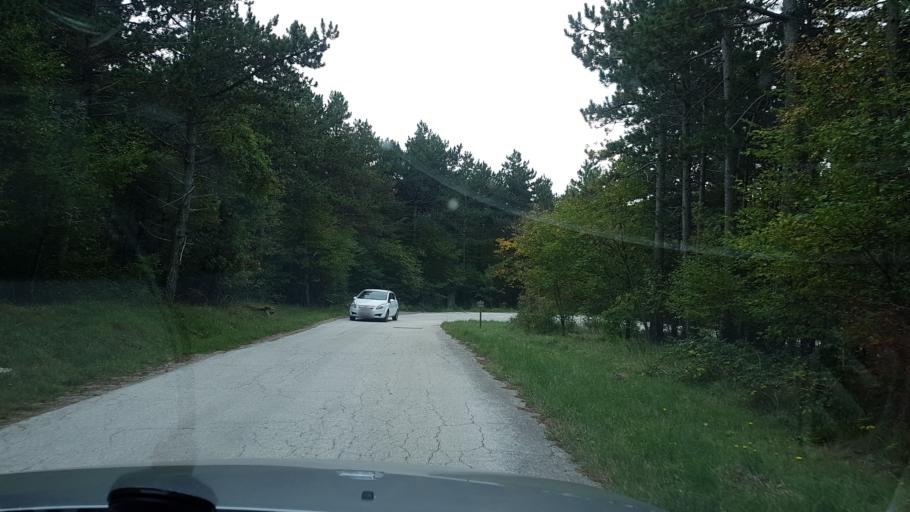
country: HR
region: Istarska
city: Buzet
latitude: 45.4519
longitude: 14.0186
